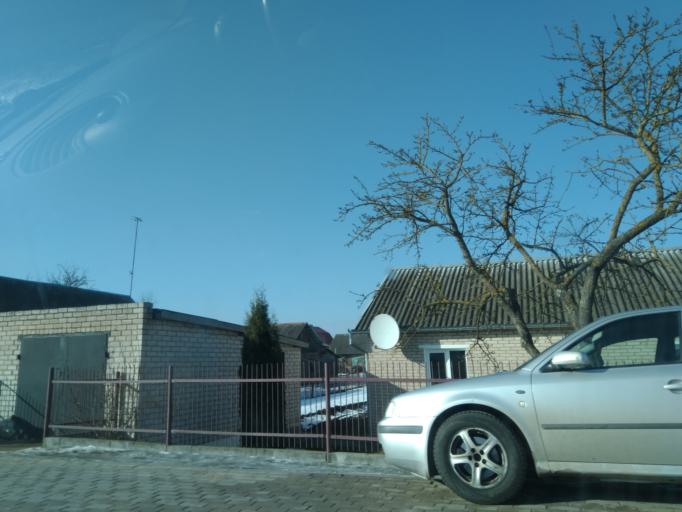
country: BY
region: Minsk
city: Nyasvizh
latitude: 53.2114
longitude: 26.6652
